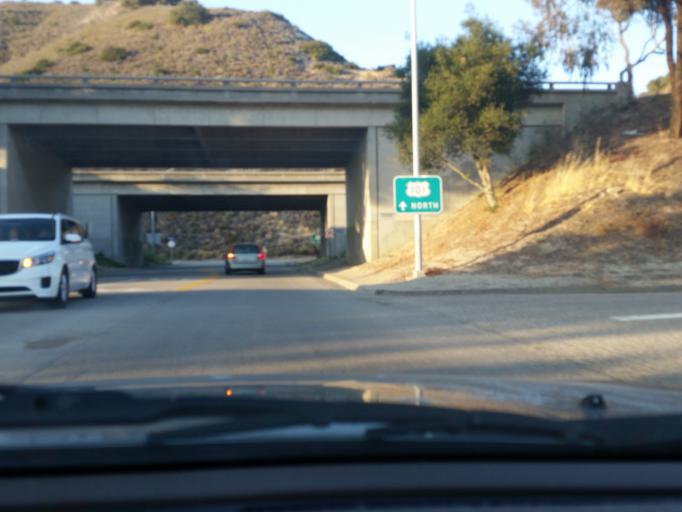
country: US
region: California
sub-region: San Luis Obispo County
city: Avila Beach
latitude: 35.1638
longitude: -120.6875
